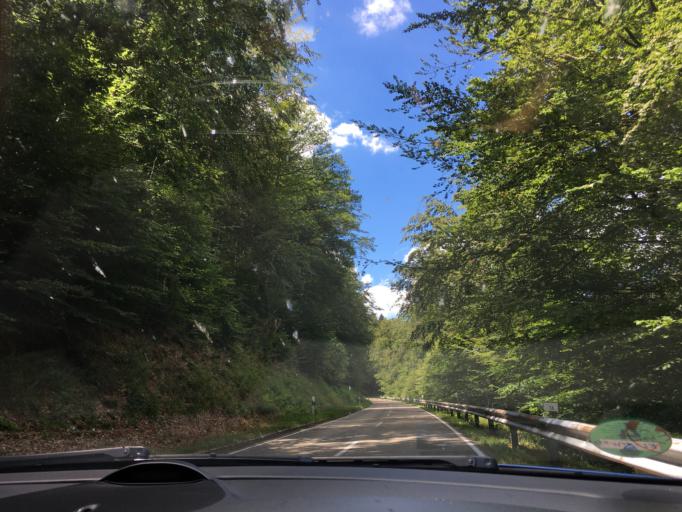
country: DE
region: Rheinland-Pfalz
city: Hauenstein
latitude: 49.2072
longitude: 7.8440
